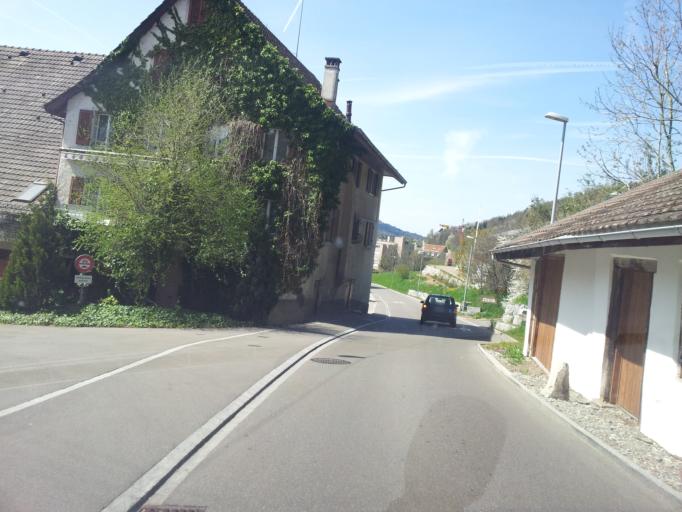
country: CH
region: Zurich
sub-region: Bezirk Dietikon
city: Geroldswil
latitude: 47.4291
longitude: 8.3951
